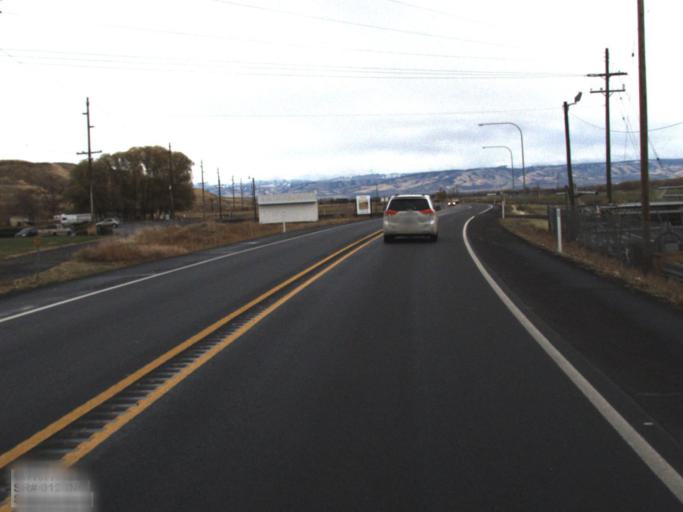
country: US
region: Washington
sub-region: Walla Walla County
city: Garrett
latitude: 46.0562
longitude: -118.5830
